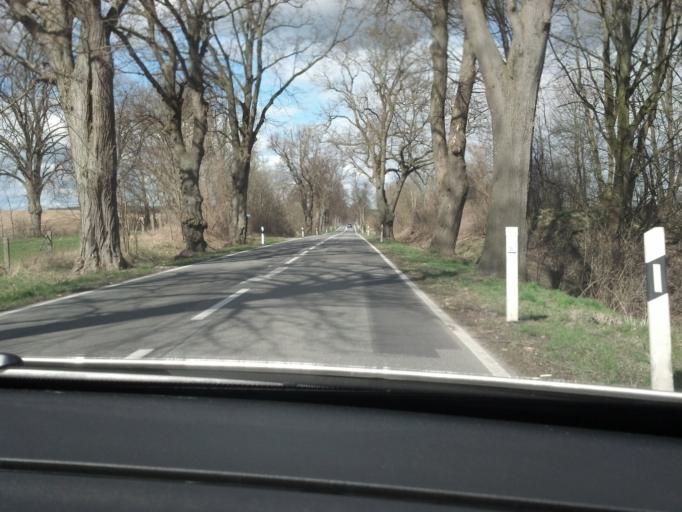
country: DE
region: Mecklenburg-Vorpommern
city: Loitz
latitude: 53.4599
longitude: 13.3605
